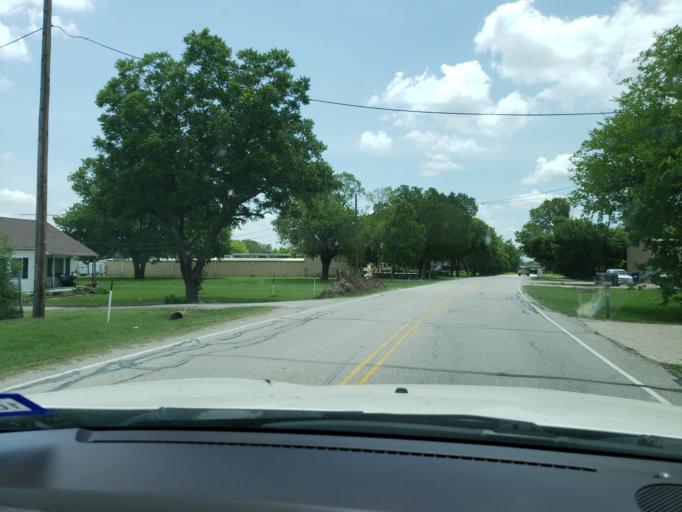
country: US
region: Texas
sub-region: Dallas County
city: Rowlett
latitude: 32.9061
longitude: -96.5756
